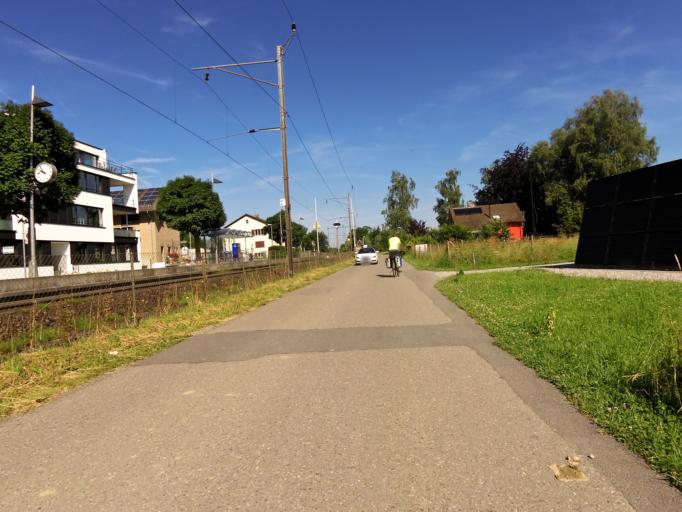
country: CH
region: Thurgau
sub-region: Kreuzlingen District
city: Bottighofen
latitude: 47.6406
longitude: 9.2136
